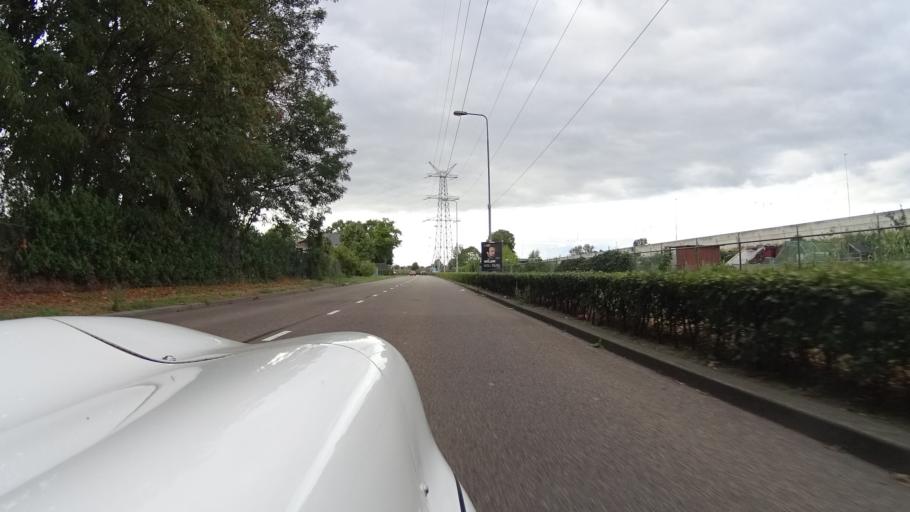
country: NL
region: North Brabant
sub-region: Gemeente 's-Hertogenbosch
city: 's-Hertogenbosch
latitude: 51.7023
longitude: 5.3487
